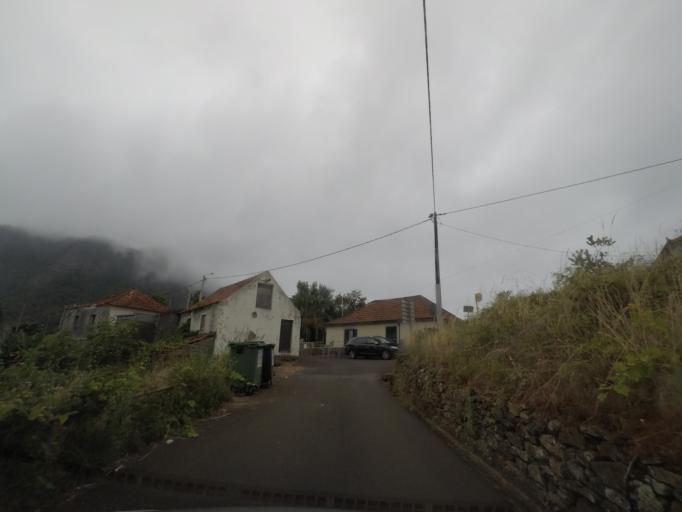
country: PT
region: Madeira
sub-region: Santana
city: Santana
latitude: 32.7680
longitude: -16.8436
